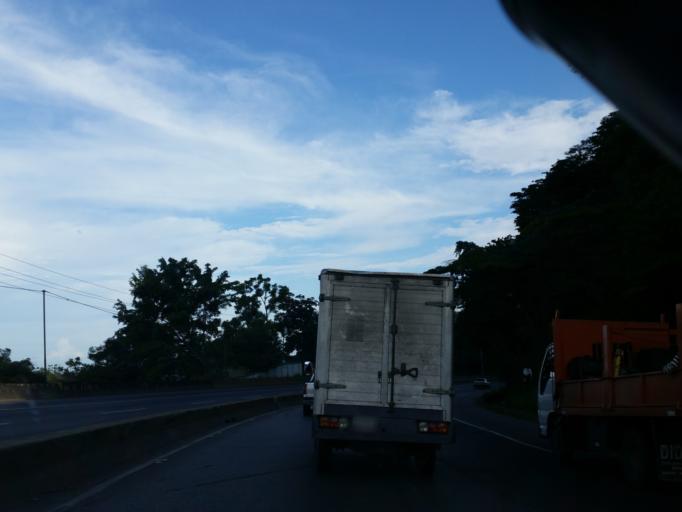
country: VE
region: Miranda
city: Caucaguita
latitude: 10.3237
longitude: -66.8727
